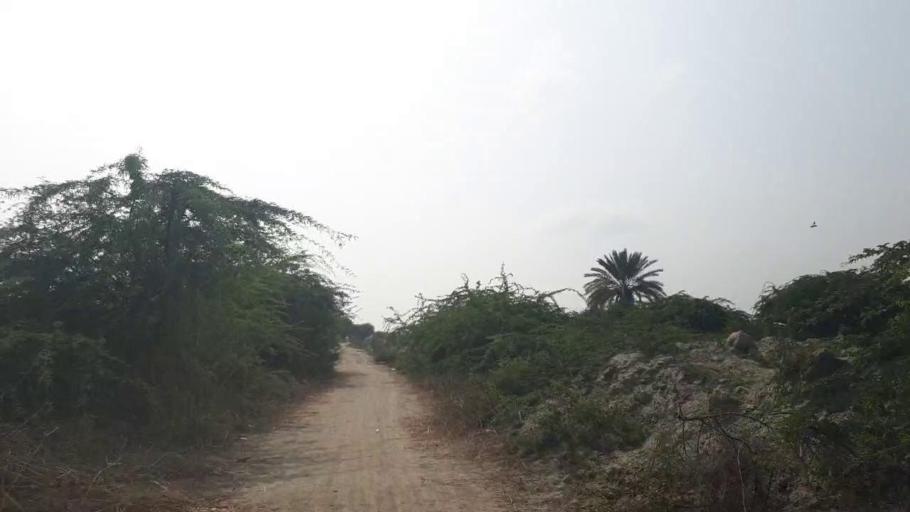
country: PK
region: Sindh
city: Badin
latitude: 24.6020
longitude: 68.7190
